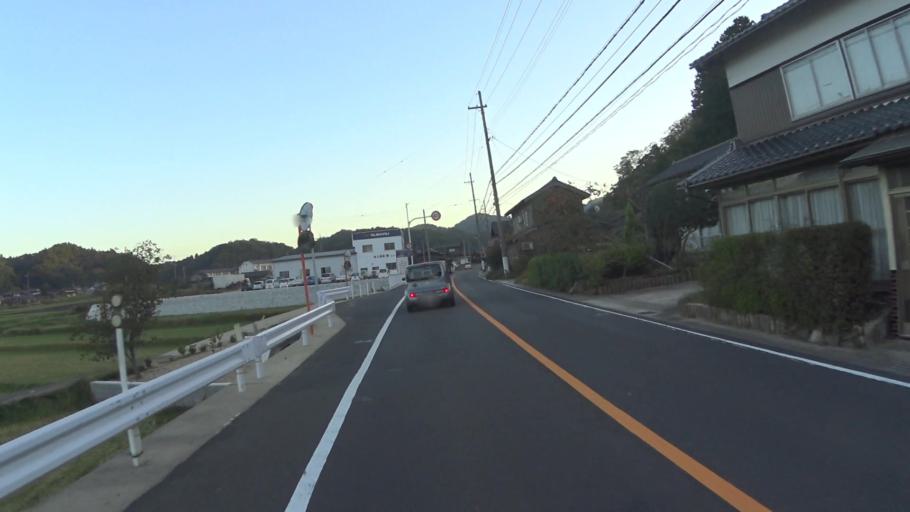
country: JP
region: Kyoto
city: Miyazu
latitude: 35.6568
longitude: 135.0326
